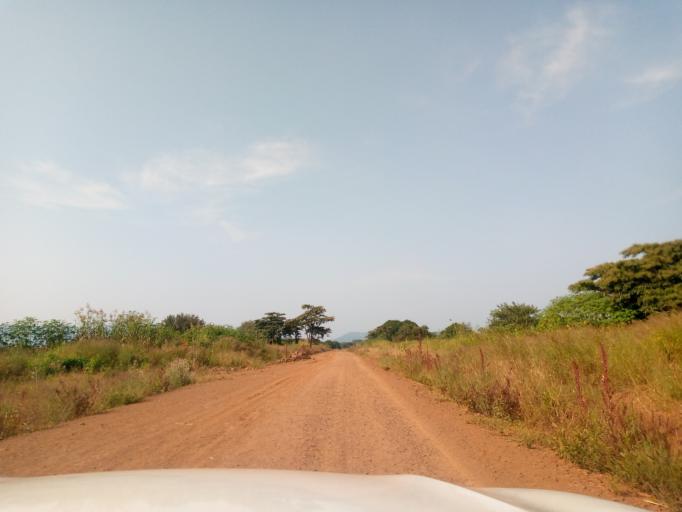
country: ET
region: Oromiya
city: Mendi
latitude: 10.1423
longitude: 34.9492
